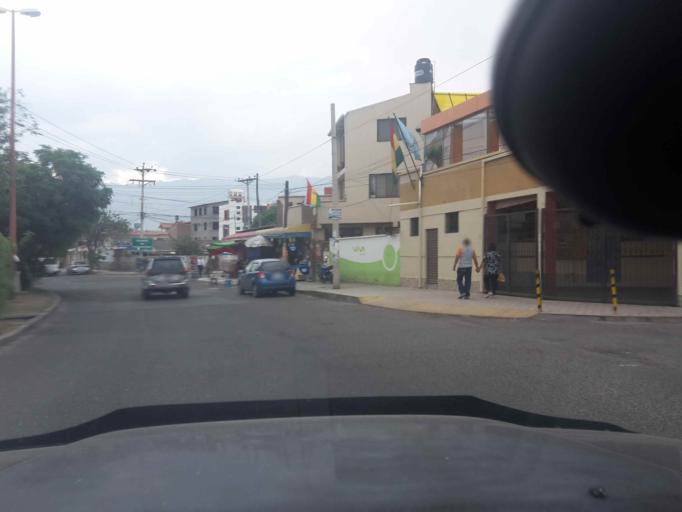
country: BO
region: Cochabamba
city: Cochabamba
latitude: -17.3817
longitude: -66.1862
